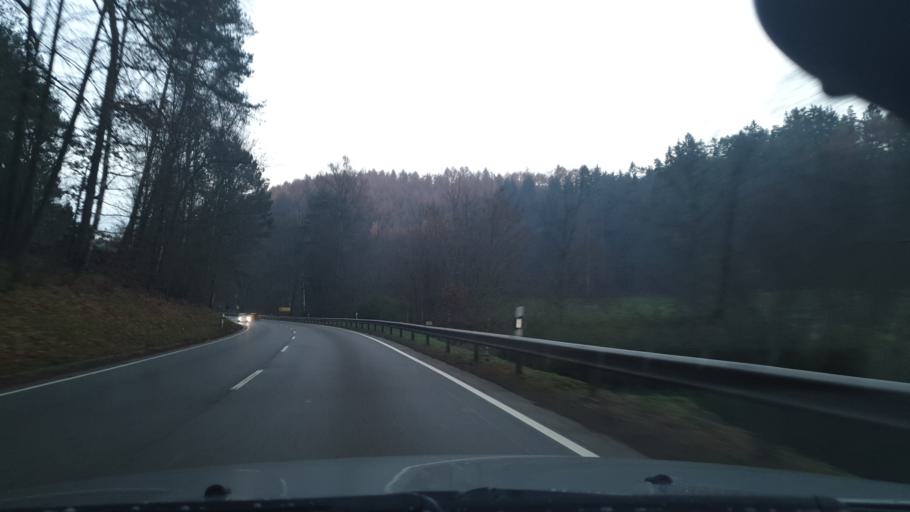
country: DE
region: Rheinland-Pfalz
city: Krickenbach
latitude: 49.3879
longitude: 7.6946
